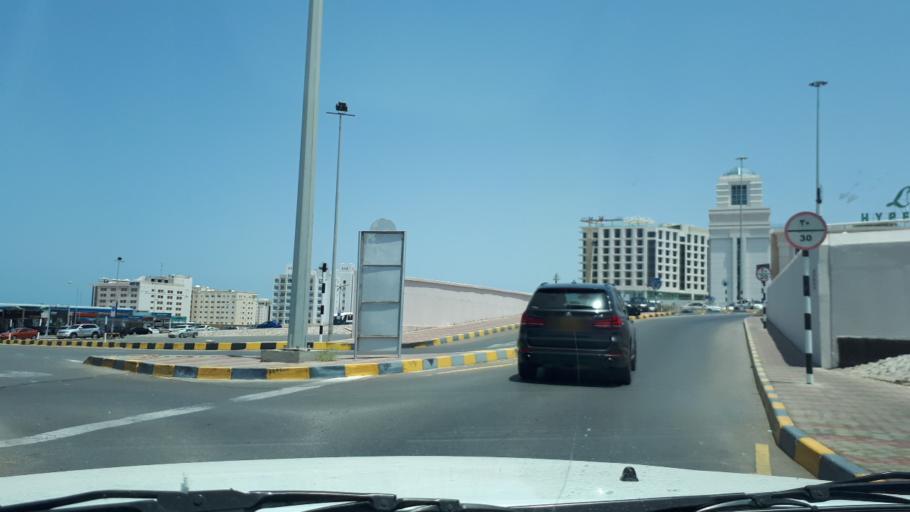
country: OM
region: Muhafazat Masqat
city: Bawshar
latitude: 23.5919
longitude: 58.4095
